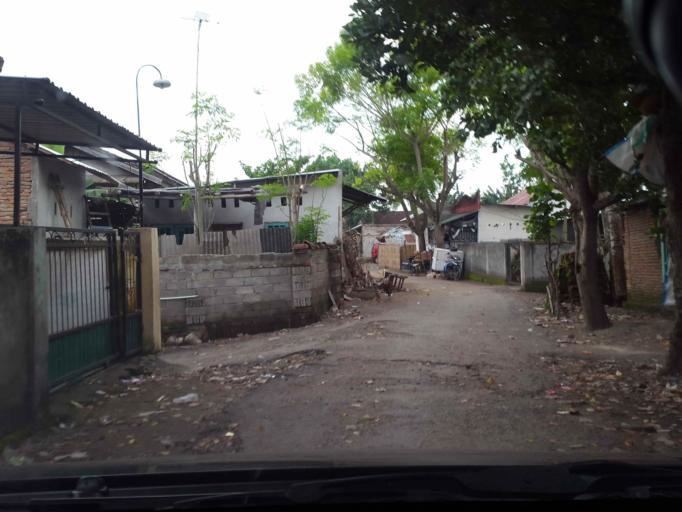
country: ID
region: West Nusa Tenggara
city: Mambalan
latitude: -8.5514
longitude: 116.0932
